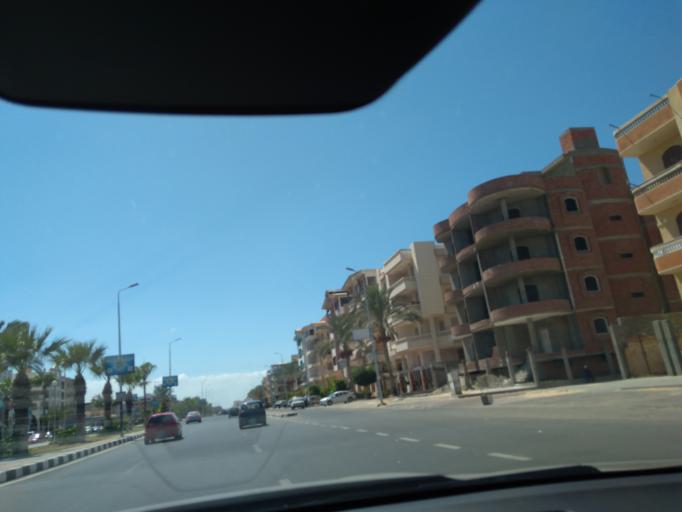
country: EG
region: Dumyat
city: Faraskur
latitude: 31.4416
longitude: 31.6829
